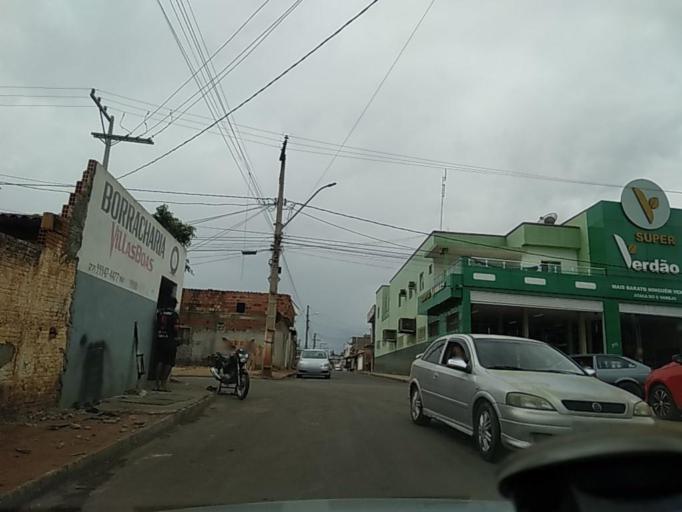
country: BR
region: Bahia
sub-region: Caetite
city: Caetite
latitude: -14.0573
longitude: -42.4801
